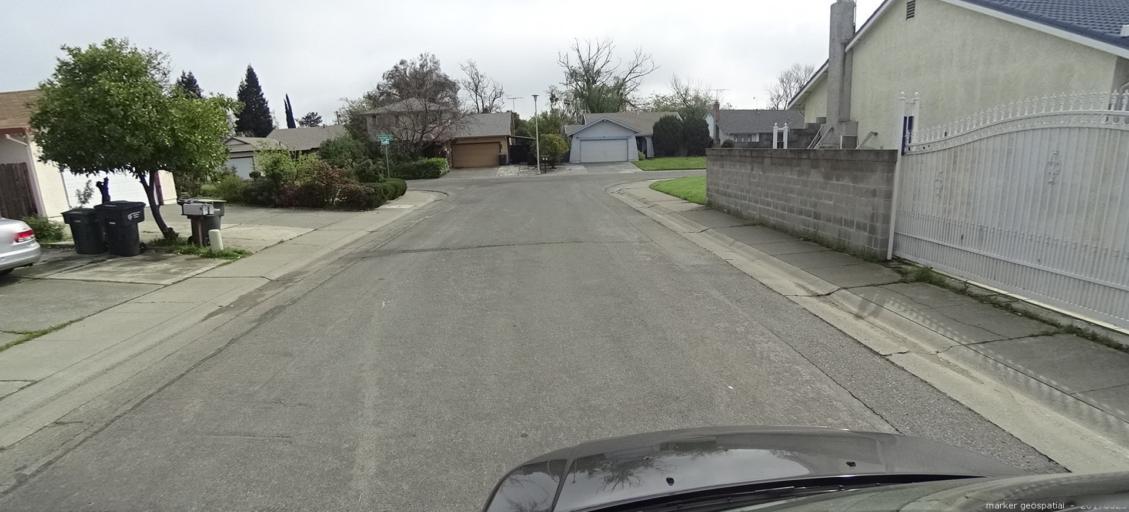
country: US
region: California
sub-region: Sacramento County
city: Florin
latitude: 38.5123
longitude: -121.4239
